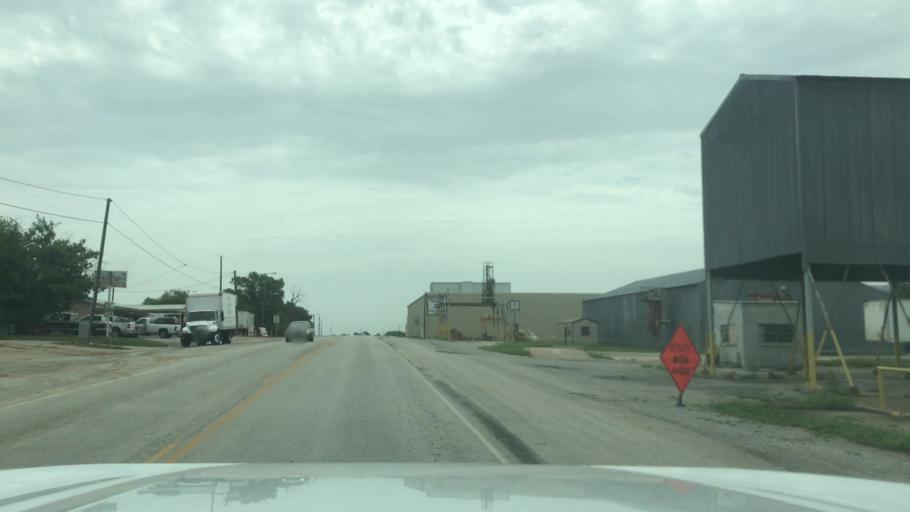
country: US
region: Texas
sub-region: Eastland County
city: Gorman
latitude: 32.2107
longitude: -98.6669
